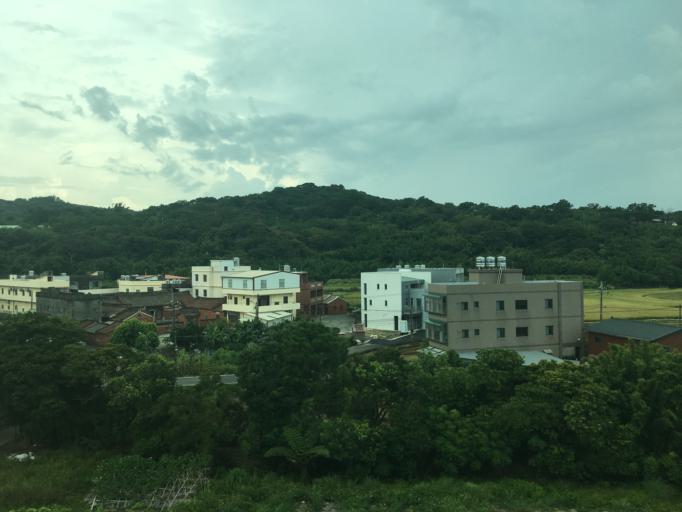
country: TW
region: Taiwan
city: Taoyuan City
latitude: 25.0806
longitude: 121.2967
